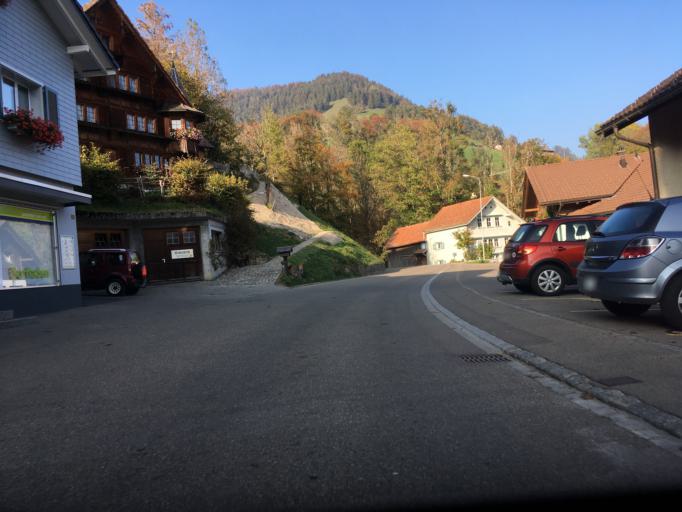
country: CH
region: Saint Gallen
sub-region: Wahlkreis Toggenburg
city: Mosnang
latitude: 47.3292
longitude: 9.0228
